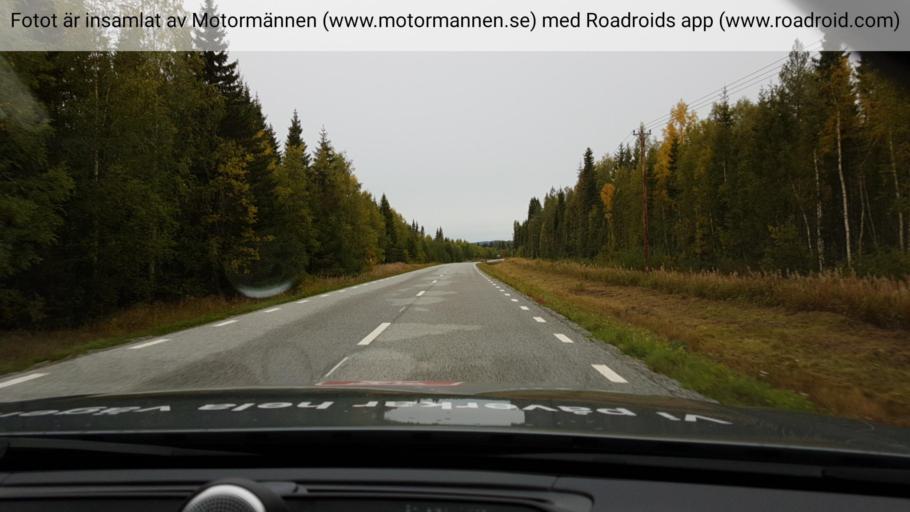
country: SE
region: Jaemtland
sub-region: Stroemsunds Kommun
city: Stroemsund
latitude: 63.9343
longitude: 15.4963
